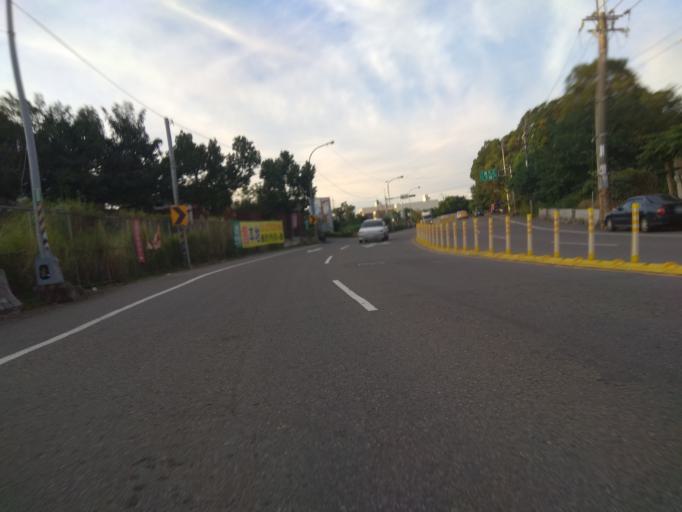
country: TW
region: Taiwan
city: Taoyuan City
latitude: 24.9769
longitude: 121.1954
